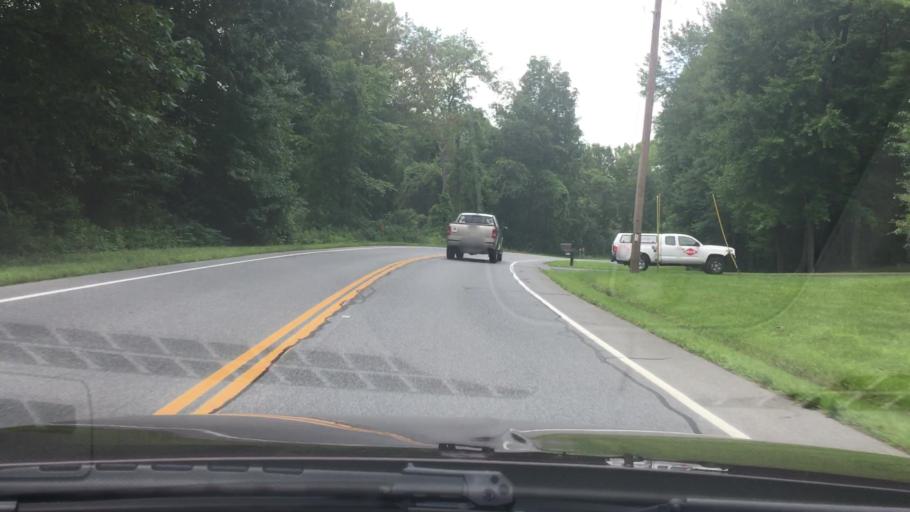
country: US
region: New York
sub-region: Dutchess County
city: Hillside Lake
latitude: 41.6465
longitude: -73.7706
